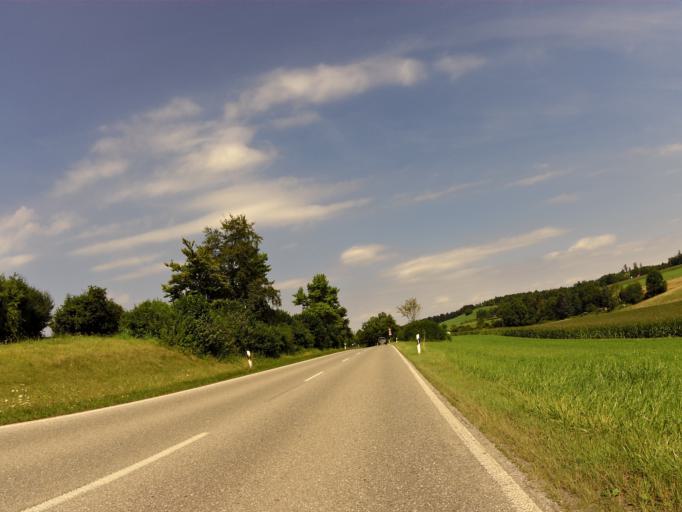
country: DE
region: Bavaria
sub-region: Upper Bavaria
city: Herrsching am Ammersee
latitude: 48.0290
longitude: 11.1405
